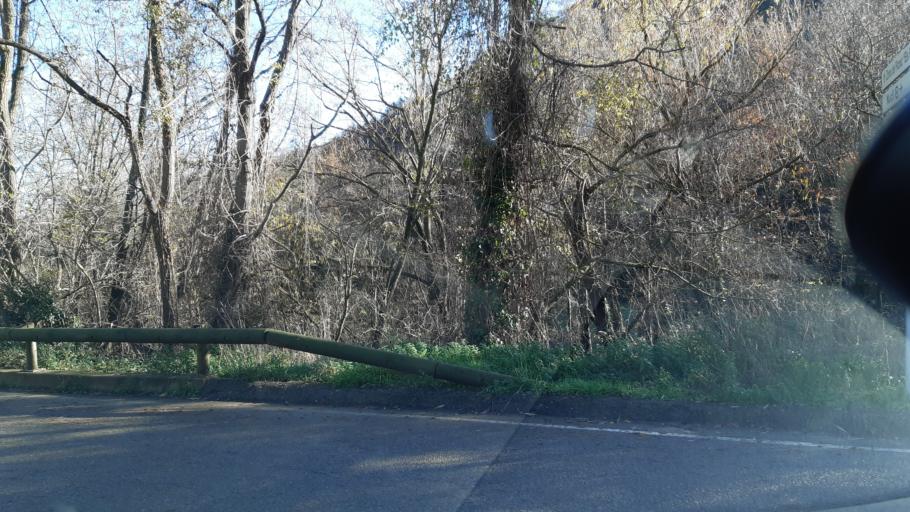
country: ES
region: Catalonia
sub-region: Provincia de Girona
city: Bas
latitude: 42.1492
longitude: 2.4094
